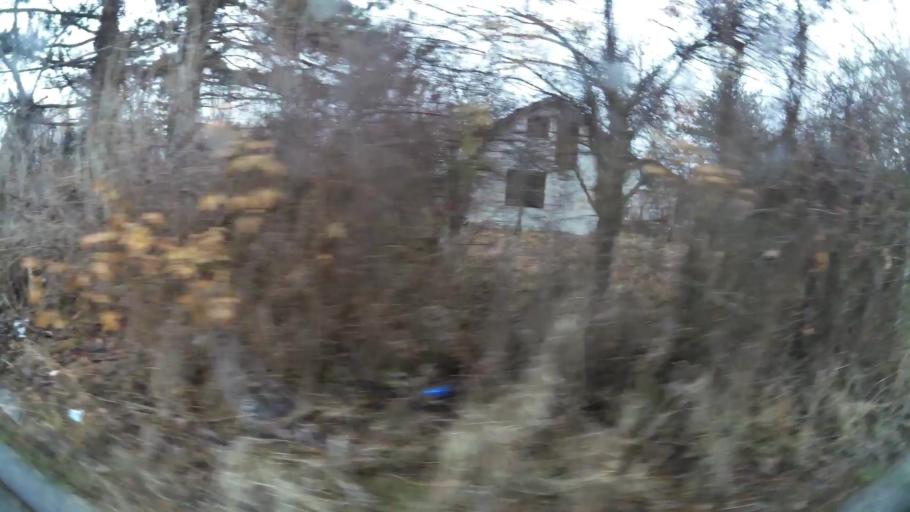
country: BG
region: Sofia-Capital
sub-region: Stolichna Obshtina
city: Sofia
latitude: 42.5996
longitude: 23.3947
